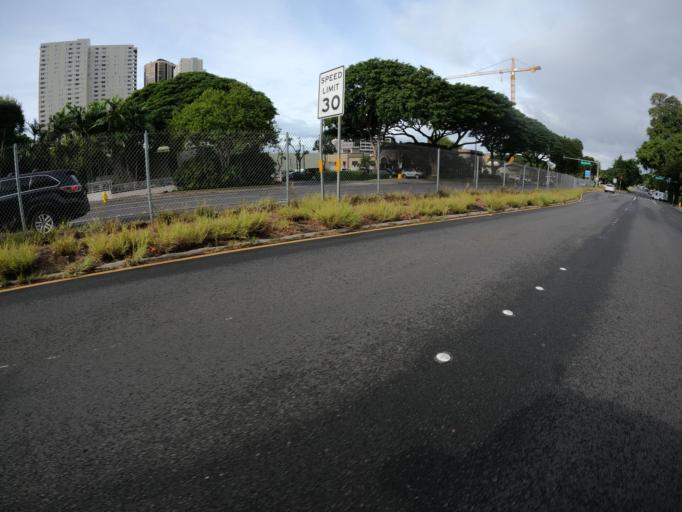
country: US
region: Hawaii
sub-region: Honolulu County
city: Honolulu
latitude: 21.3149
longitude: -157.8580
